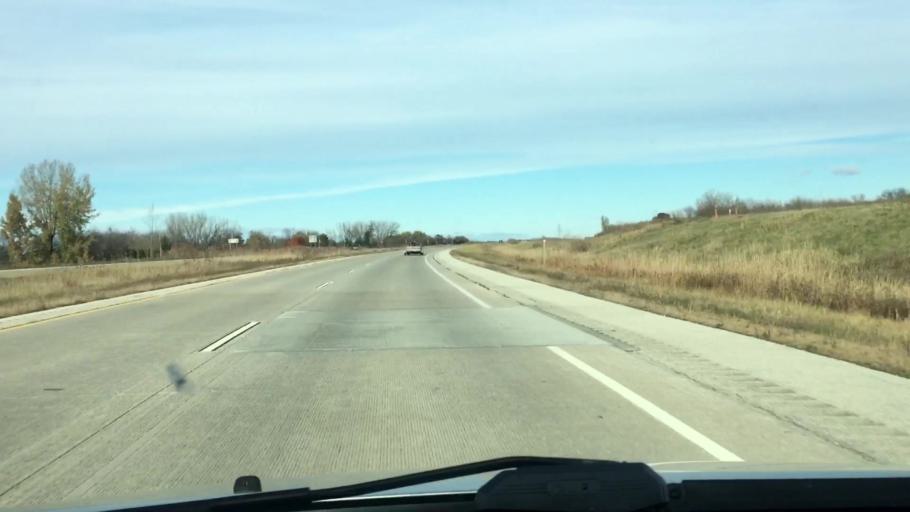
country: US
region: Wisconsin
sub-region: Kewaunee County
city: Luxemburg
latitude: 44.6487
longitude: -87.7524
